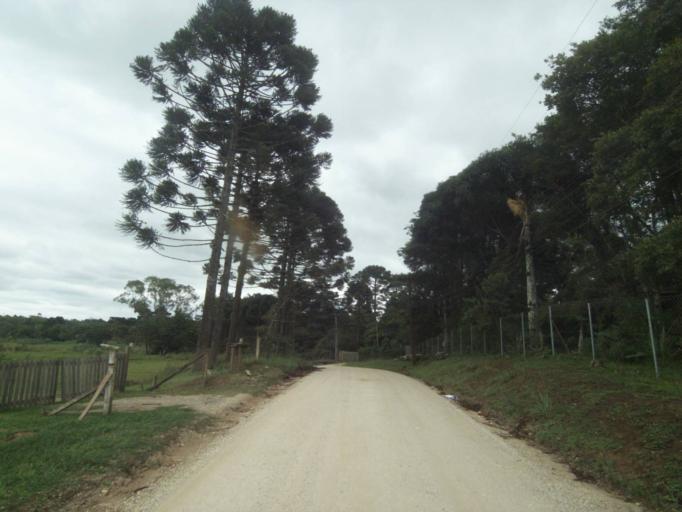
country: BR
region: Parana
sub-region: Campina Grande Do Sul
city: Campina Grande do Sul
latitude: -25.3263
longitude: -49.0898
